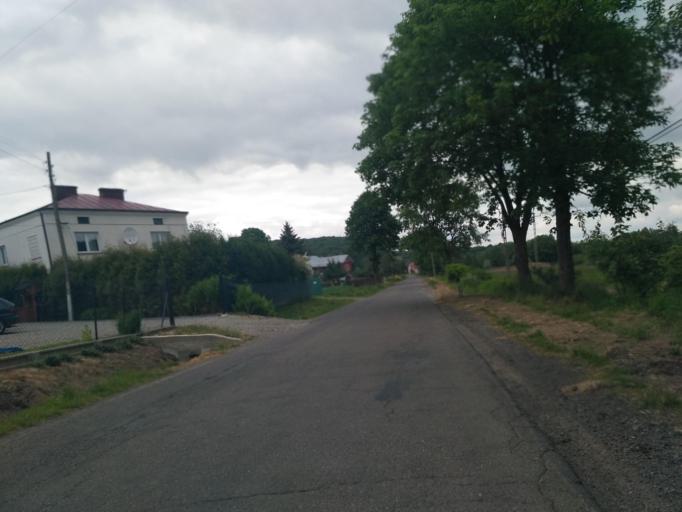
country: PL
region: Subcarpathian Voivodeship
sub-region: Powiat jasielski
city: Tarnowiec
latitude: 49.6873
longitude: 21.5987
